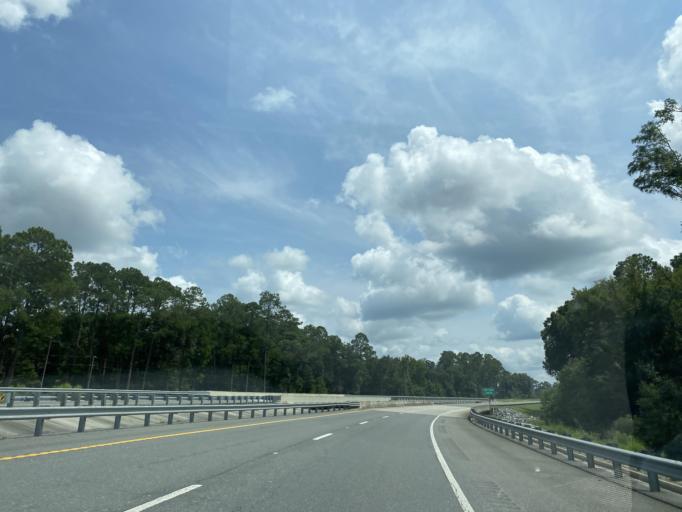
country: US
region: Georgia
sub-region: Ware County
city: Deenwood
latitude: 31.3197
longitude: -82.4577
